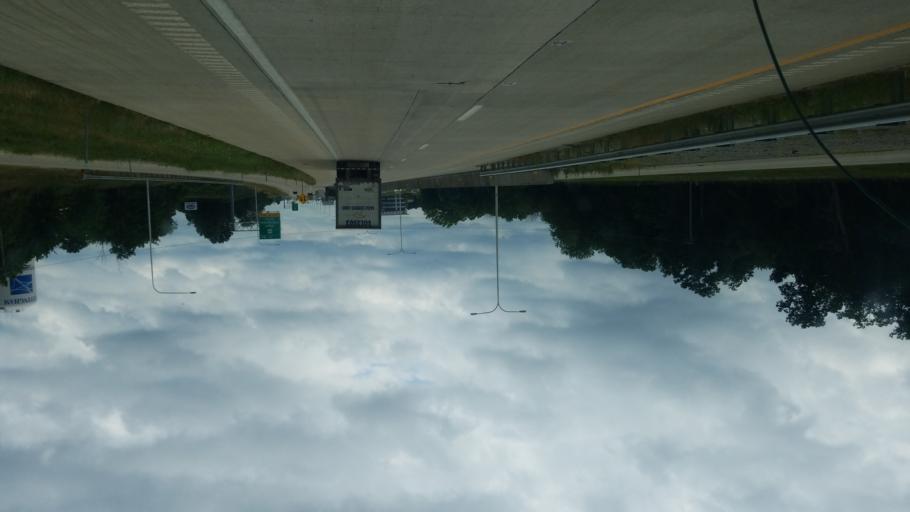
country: US
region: Illinois
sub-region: Effingham County
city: Effingham
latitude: 39.1482
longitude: -88.5151
